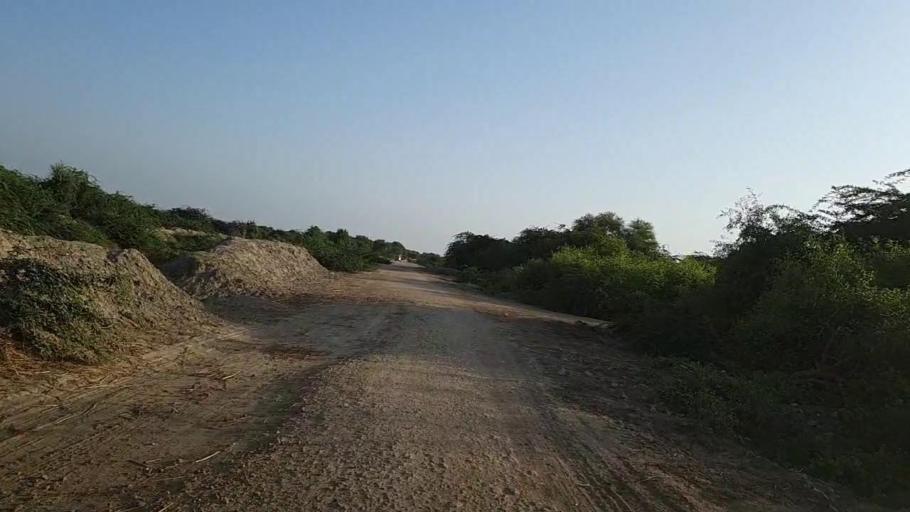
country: PK
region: Sindh
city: Kario
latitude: 24.7188
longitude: 68.6673
